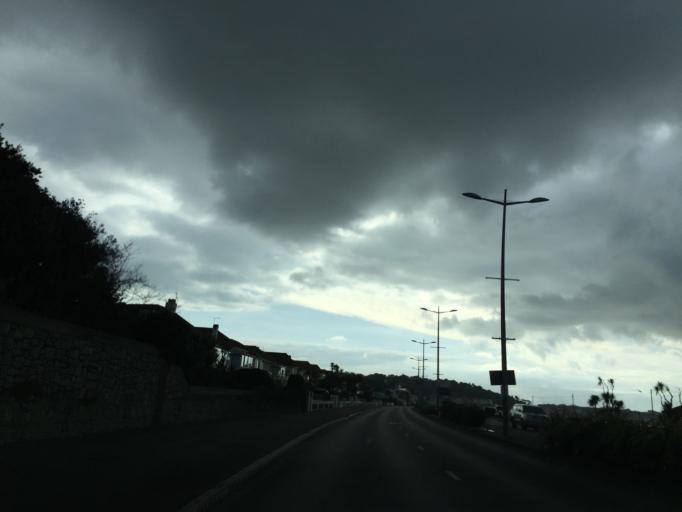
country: JE
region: St Helier
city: Saint Helier
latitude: 49.1967
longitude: -2.1375
